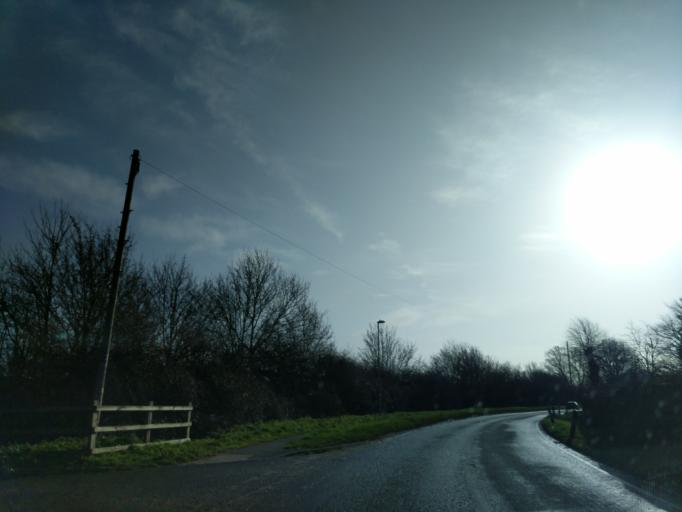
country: GB
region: England
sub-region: Cambridgeshire
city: Hemingford Grey
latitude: 52.3155
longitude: -0.0759
